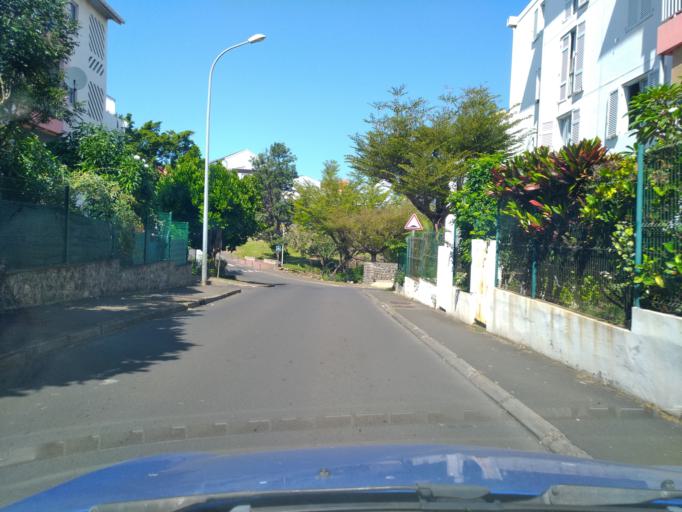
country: RE
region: Reunion
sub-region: Reunion
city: Saint-Pierre
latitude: -21.3327
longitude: 55.4738
